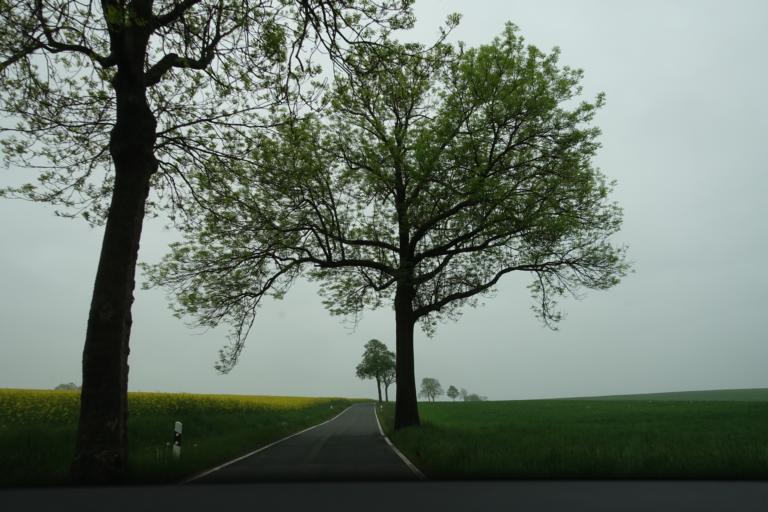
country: DE
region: Saxony
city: Grosshartmannsdorf
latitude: 50.8205
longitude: 13.2993
